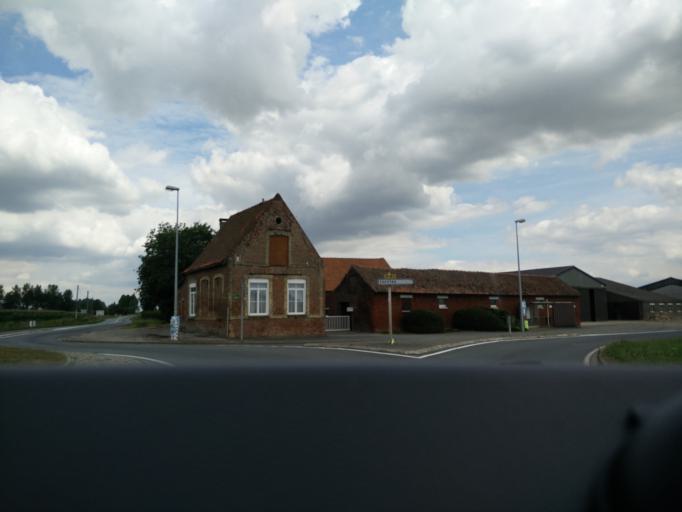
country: FR
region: Nord-Pas-de-Calais
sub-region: Departement du Nord
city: Saint-Sylvestre-Cappel
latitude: 50.7522
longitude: 2.5532
